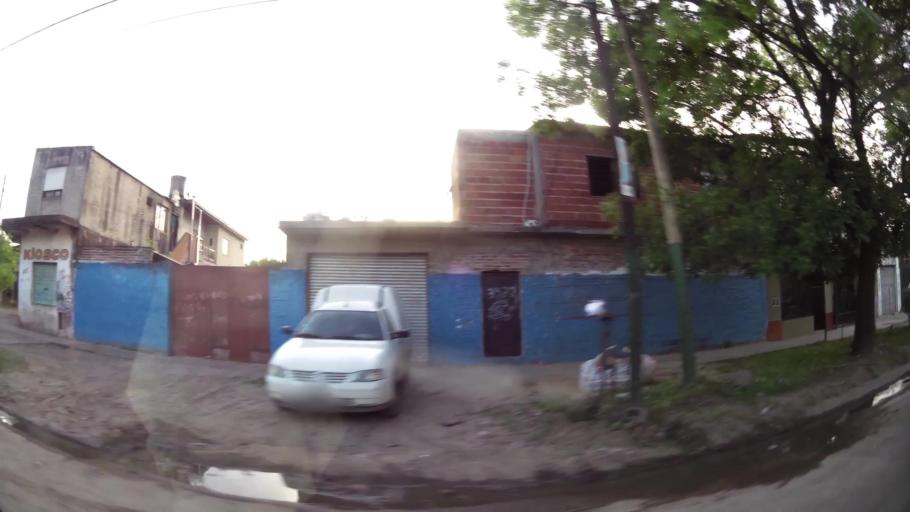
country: AR
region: Buenos Aires
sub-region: Partido de Almirante Brown
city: Adrogue
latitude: -34.7804
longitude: -58.3189
